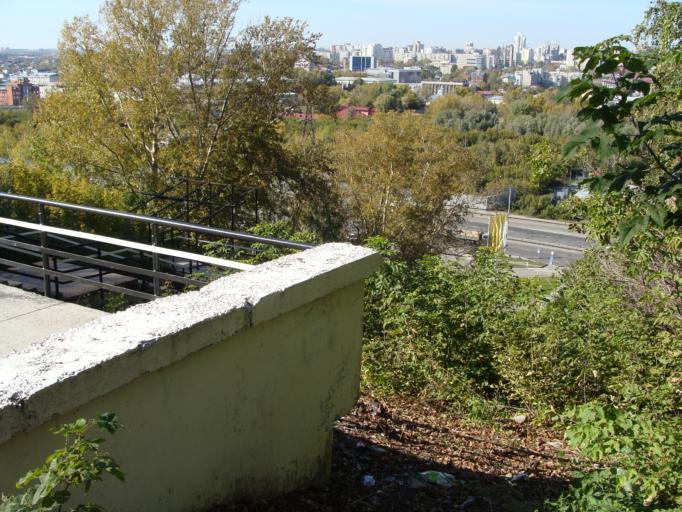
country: RU
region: Altai Krai
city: Zaton
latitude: 53.3249
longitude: 83.7947
